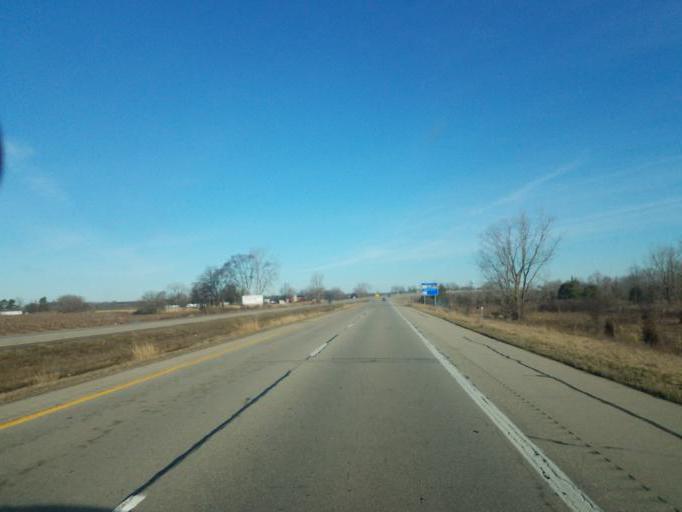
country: US
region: Michigan
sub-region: Gratiot County
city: Ithaca
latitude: 43.2804
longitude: -84.5765
